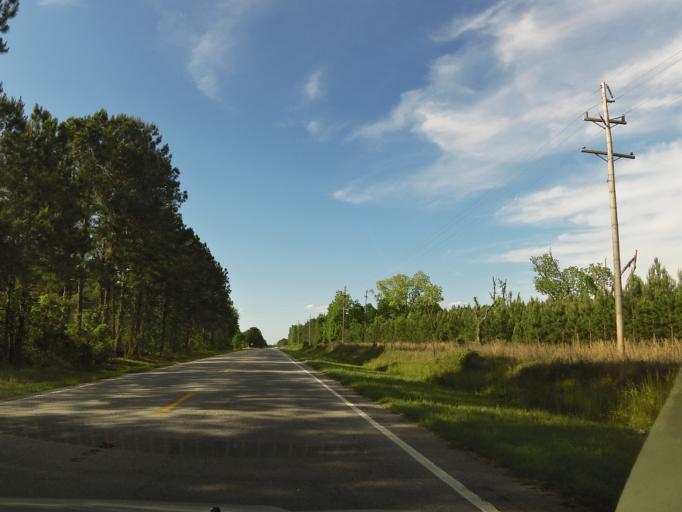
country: US
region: South Carolina
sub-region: Allendale County
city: Fairfax
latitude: 32.9184
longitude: -81.2374
